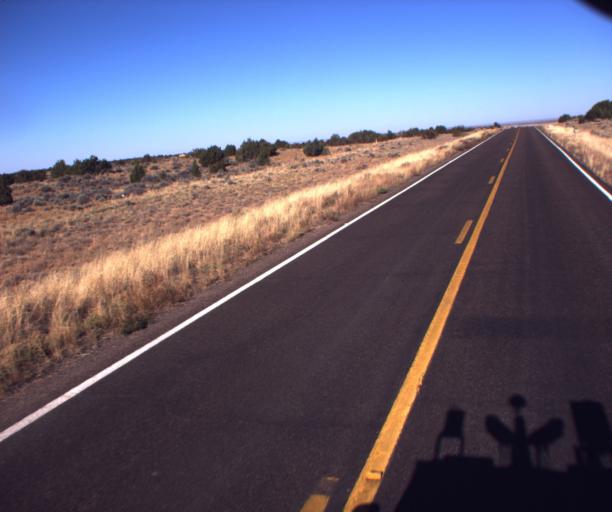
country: US
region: Arizona
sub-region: Navajo County
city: First Mesa
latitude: 35.7930
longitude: -110.1863
